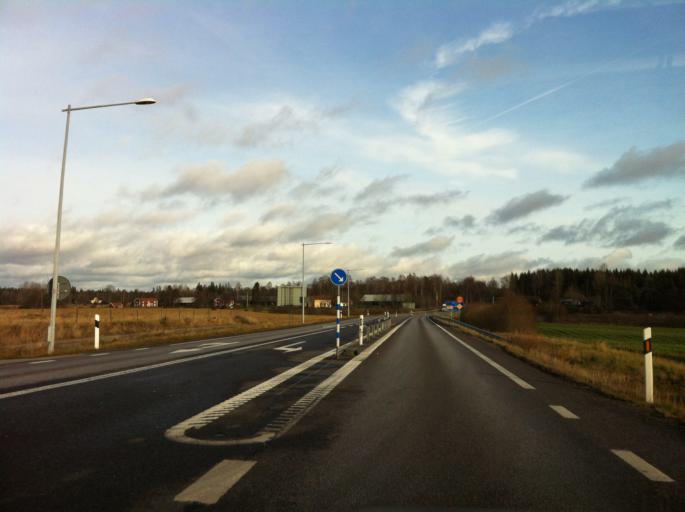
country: SE
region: Kronoberg
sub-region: Almhults Kommun
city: AElmhult
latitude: 56.6600
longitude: 14.2920
